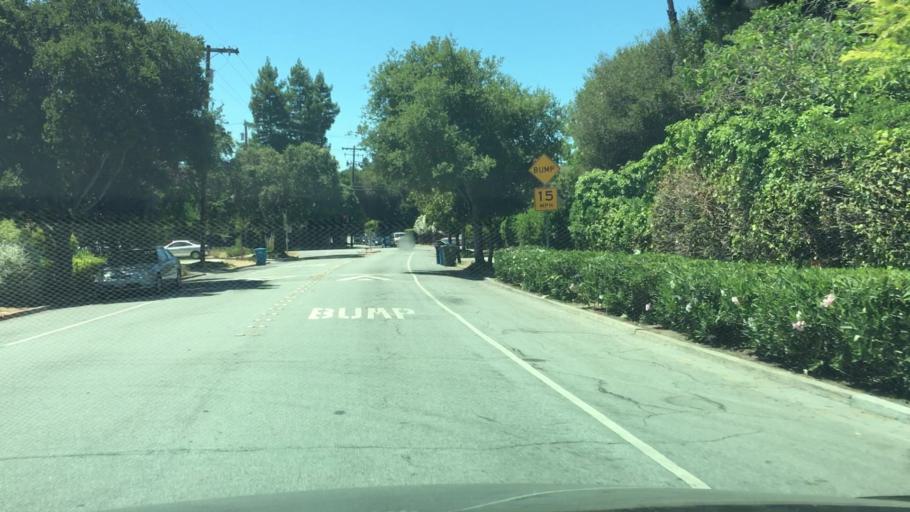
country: US
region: California
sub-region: San Mateo County
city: Redwood City
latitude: 37.4835
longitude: -122.2548
